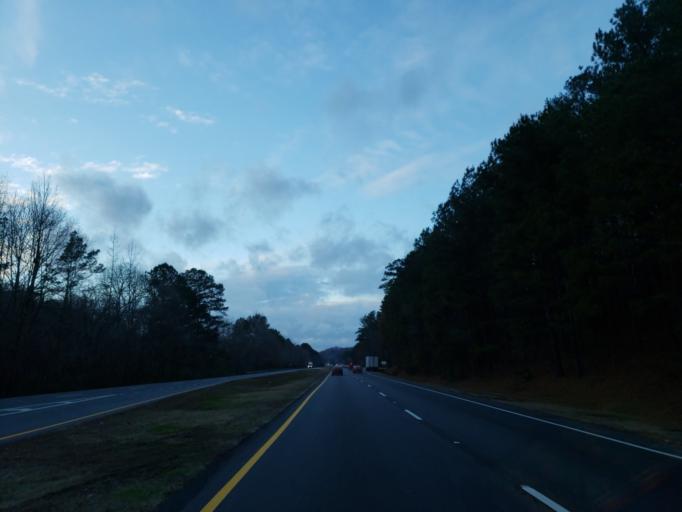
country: US
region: Georgia
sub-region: Fulton County
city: Union City
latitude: 33.6627
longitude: -84.5391
